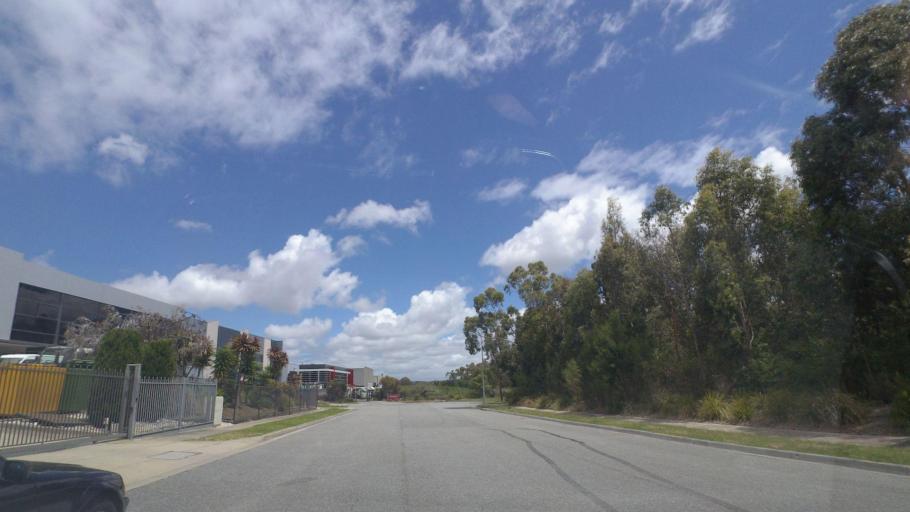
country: AU
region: Victoria
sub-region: Knox
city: Scoresby
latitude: -37.9053
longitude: 145.2425
